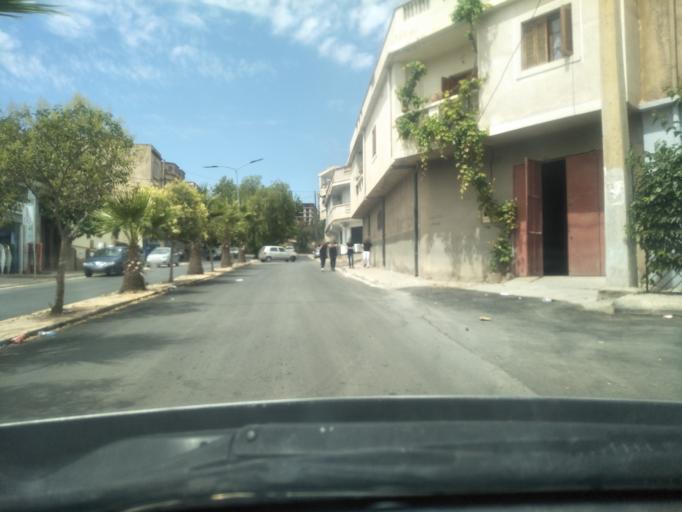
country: DZ
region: Tlemcen
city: Tlemcen
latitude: 34.9029
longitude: -1.3259
